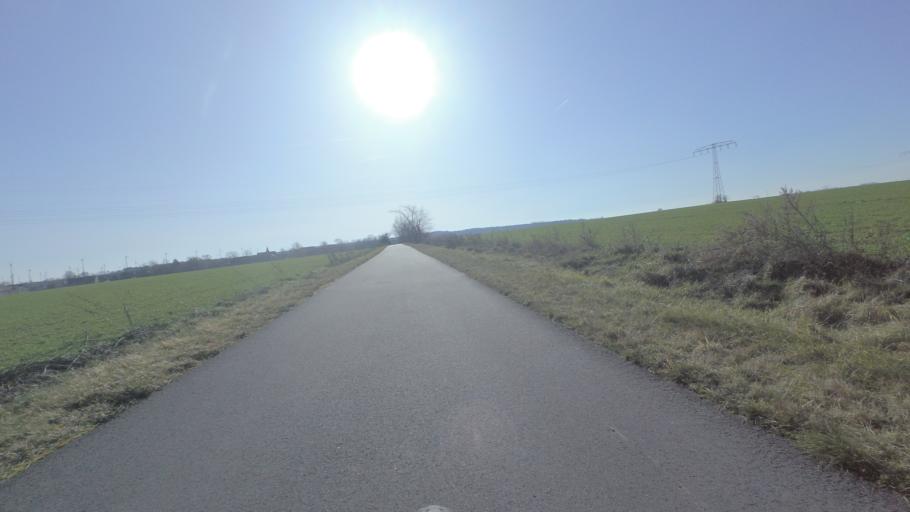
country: DE
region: Brandenburg
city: Luckenwalde
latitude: 52.0445
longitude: 13.1349
